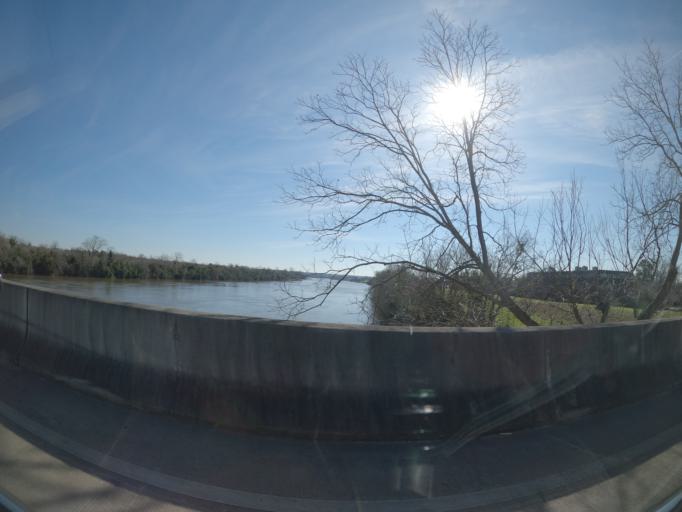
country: US
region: Georgia
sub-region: Richmond County
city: Augusta
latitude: 33.4749
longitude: -81.9556
